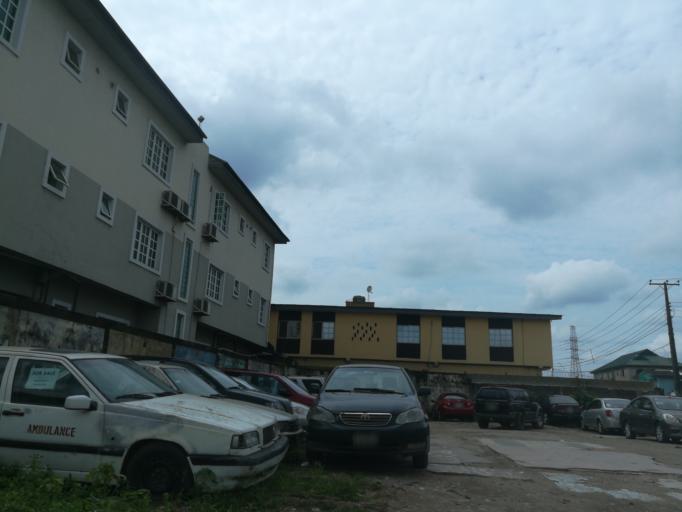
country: NG
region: Lagos
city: Somolu
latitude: 6.5484
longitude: 3.3927
